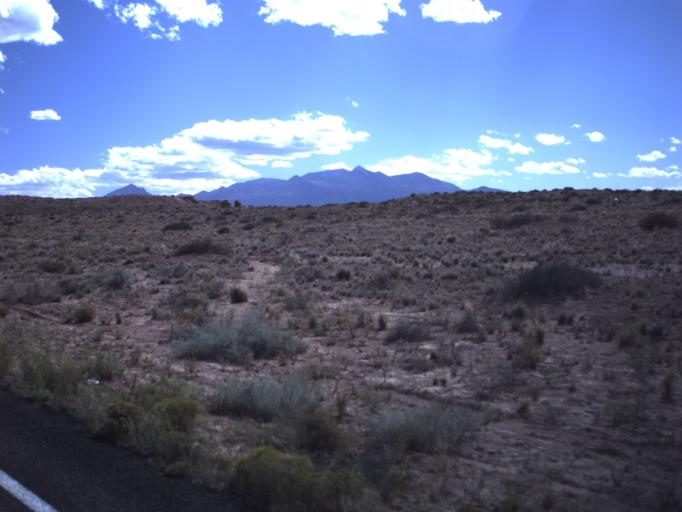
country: US
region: Utah
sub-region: Emery County
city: Ferron
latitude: 38.3624
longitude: -110.6998
